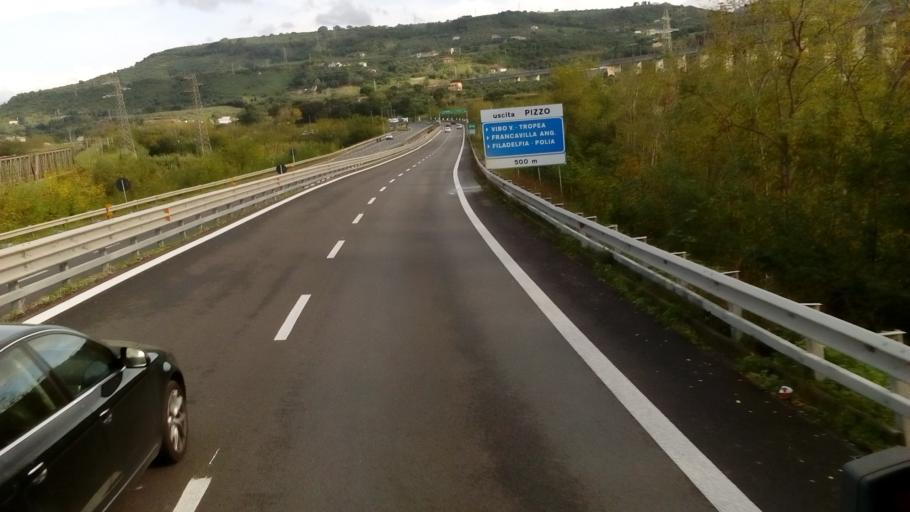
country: IT
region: Calabria
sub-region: Provincia di Vibo-Valentia
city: Pizzo
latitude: 38.7695
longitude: 16.2092
